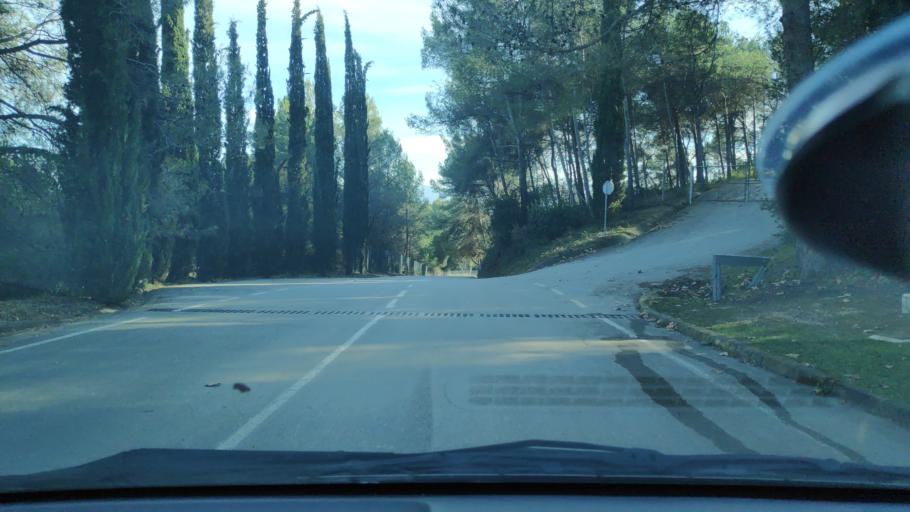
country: ES
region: Catalonia
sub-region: Provincia de Barcelona
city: Rubi
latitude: 41.4980
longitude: 2.0569
